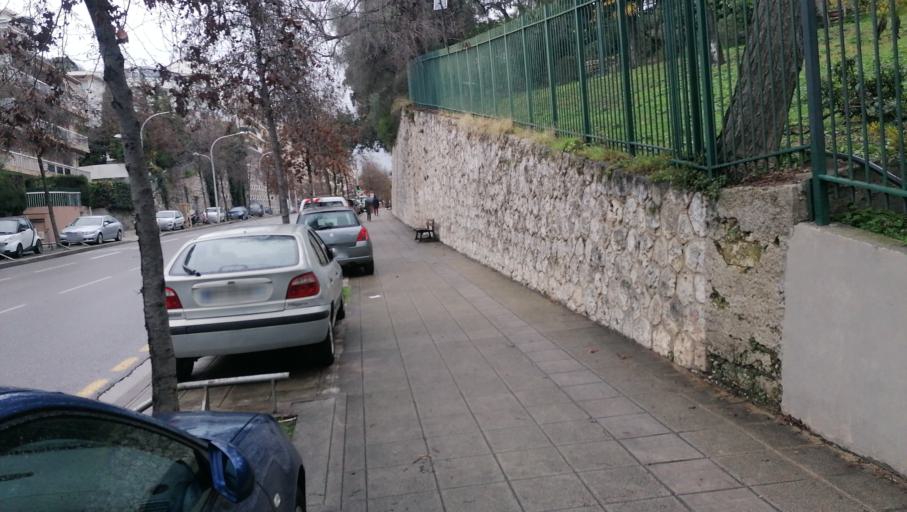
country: FR
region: Provence-Alpes-Cote d'Azur
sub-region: Departement des Alpes-Maritimes
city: Nice
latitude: 43.7139
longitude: 7.2547
